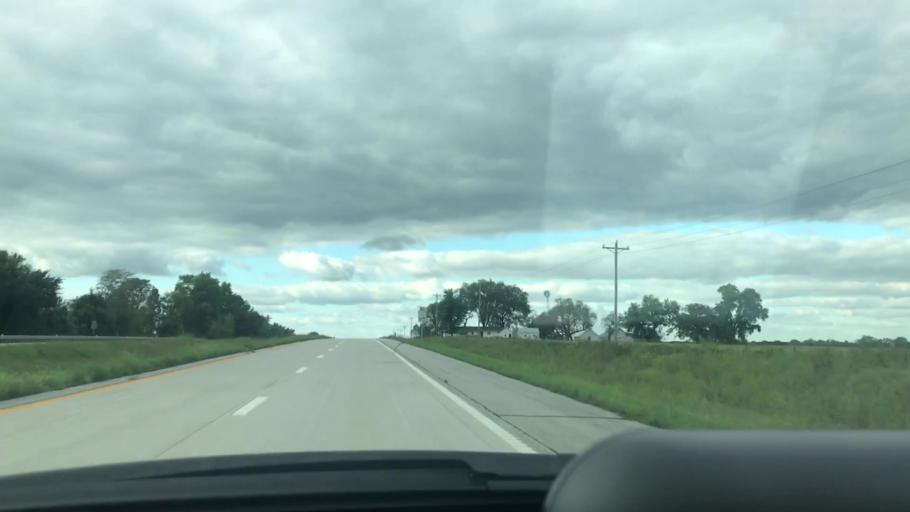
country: US
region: Missouri
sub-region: Benton County
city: Lincoln
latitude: 38.3669
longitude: -93.3388
